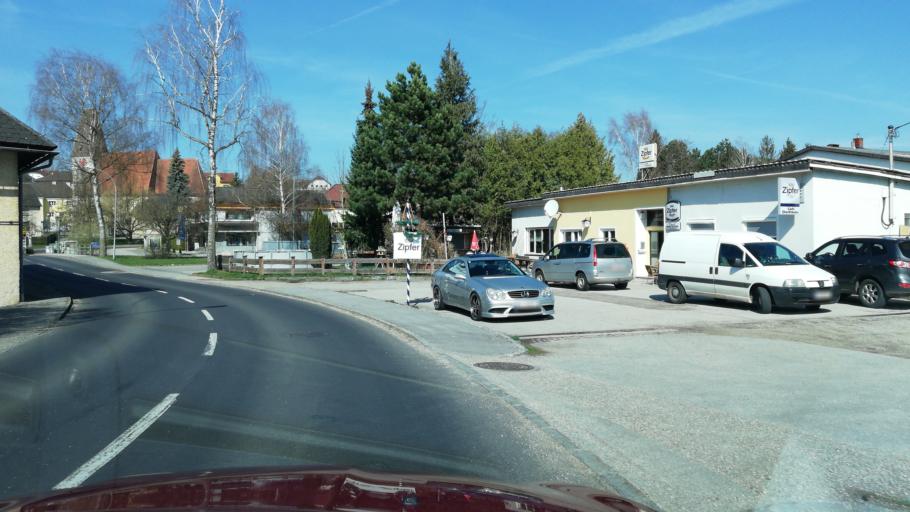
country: AT
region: Upper Austria
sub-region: Politischer Bezirk Kirchdorf an der Krems
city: Kremsmunster
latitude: 48.0970
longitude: 14.1115
